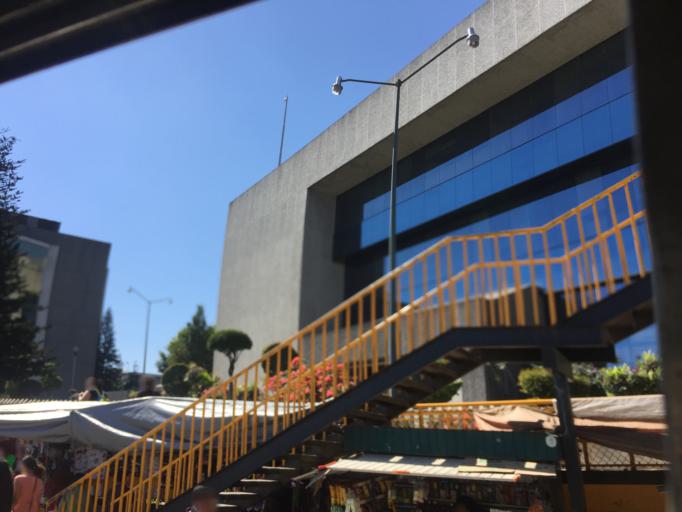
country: MX
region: Veracruz
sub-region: Xalapa
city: Xalapa de Enriquez
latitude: 19.5389
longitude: -96.9079
